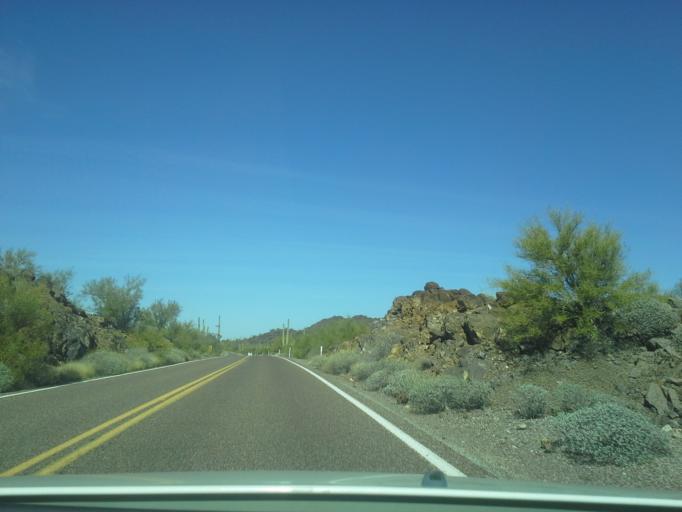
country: MX
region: Sonora
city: Sonoyta
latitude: 31.9774
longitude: -112.8057
